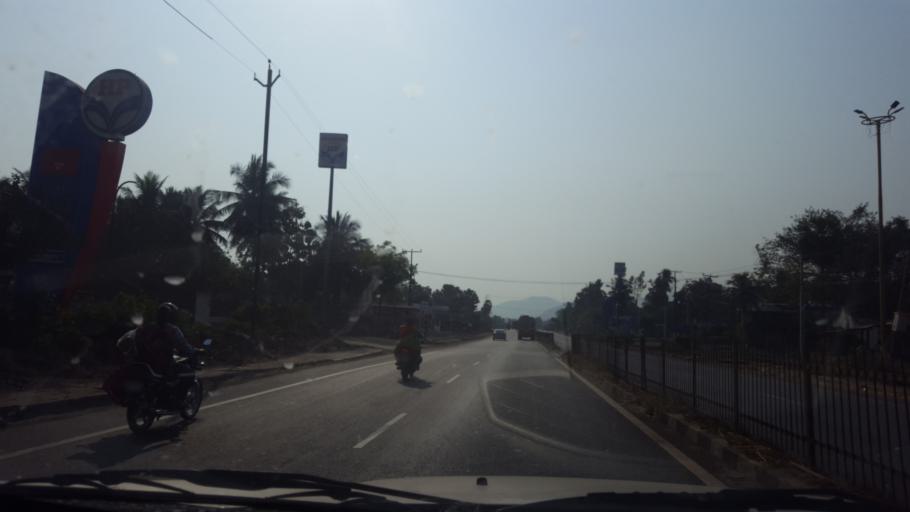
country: IN
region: Andhra Pradesh
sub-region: Vishakhapatnam
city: Anakapalle
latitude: 17.6661
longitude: 82.9535
